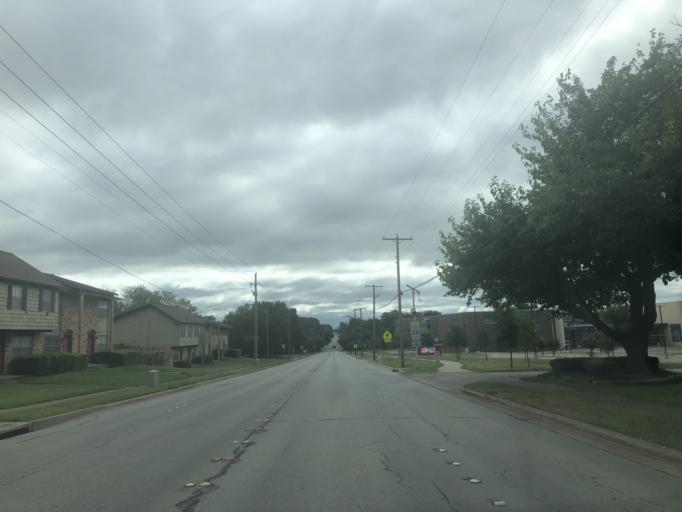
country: US
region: Texas
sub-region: Dallas County
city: Duncanville
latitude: 32.6517
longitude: -96.9235
